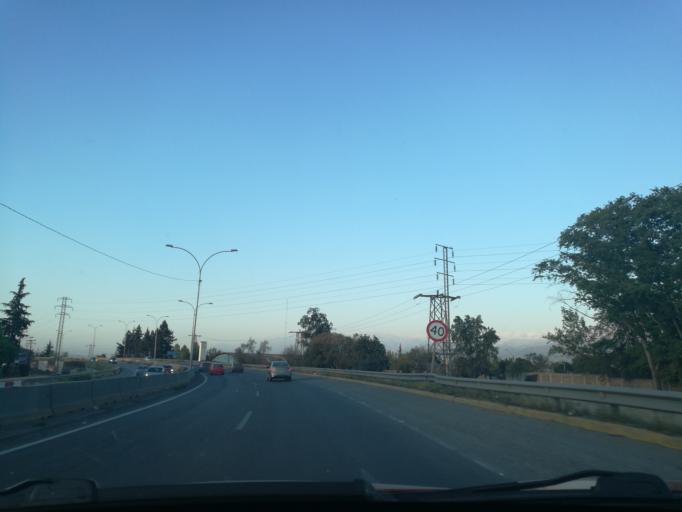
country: CL
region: O'Higgins
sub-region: Provincia de Cachapoal
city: Rancagua
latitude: -34.1748
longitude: -70.7277
